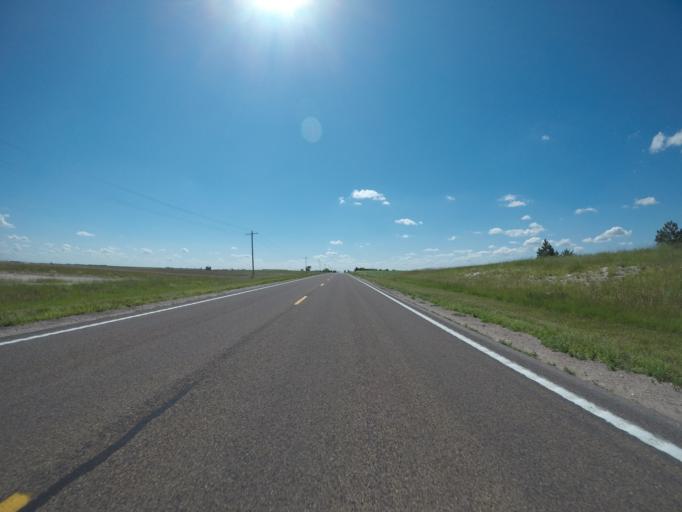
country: US
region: Nebraska
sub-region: Chase County
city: Imperial
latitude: 40.5375
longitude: -101.8292
